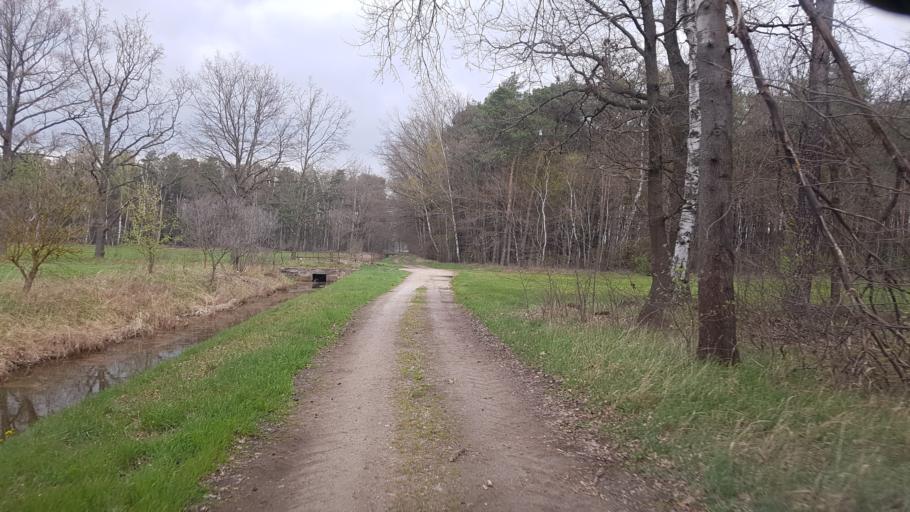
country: DE
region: Brandenburg
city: Bronkow
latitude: 51.6339
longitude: 13.8805
